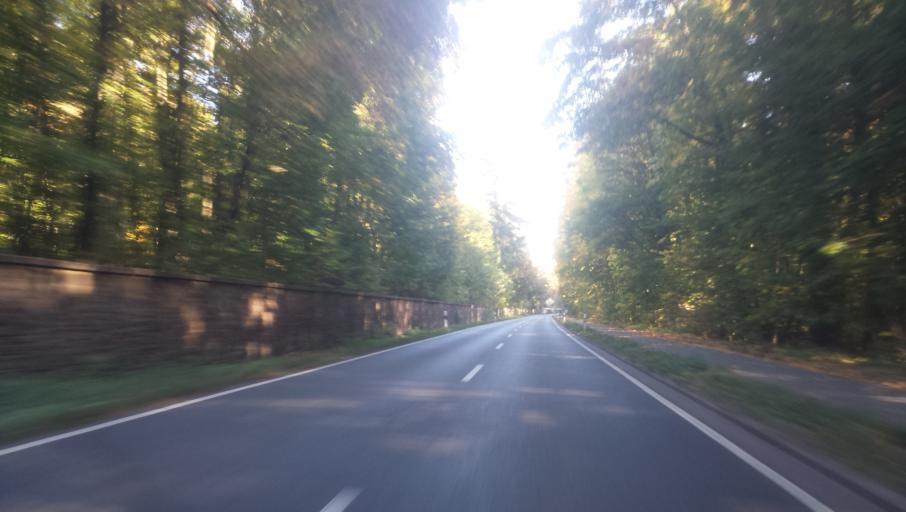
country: DE
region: Hesse
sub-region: Regierungsbezirk Darmstadt
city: Darmstadt
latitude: 49.8873
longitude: 8.6907
